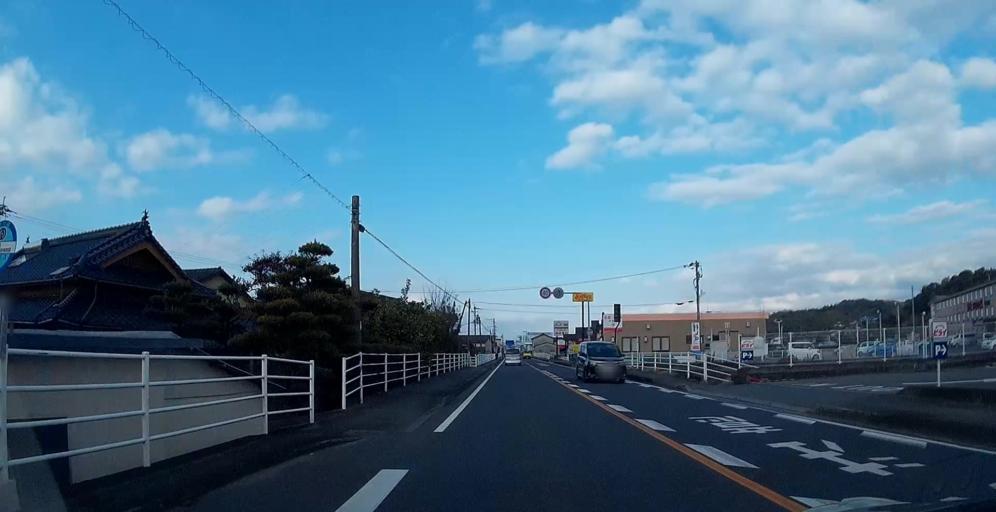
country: JP
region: Kumamoto
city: Yatsushiro
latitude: 32.5515
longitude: 130.6792
